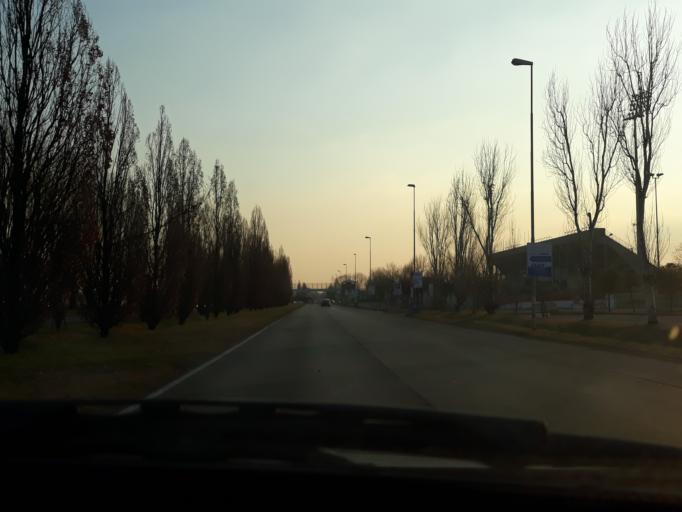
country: IT
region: Lombardy
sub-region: Provincia di Monza e Brianza
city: Villasanta
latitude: 45.5850
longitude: 9.3102
